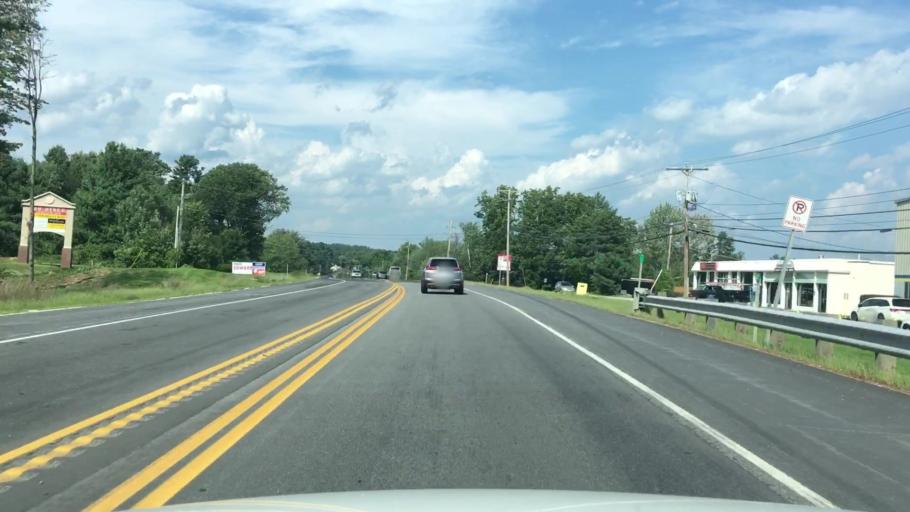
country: US
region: New Hampshire
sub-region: Rockingham County
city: Londonderry
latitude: 42.8501
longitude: -71.3581
